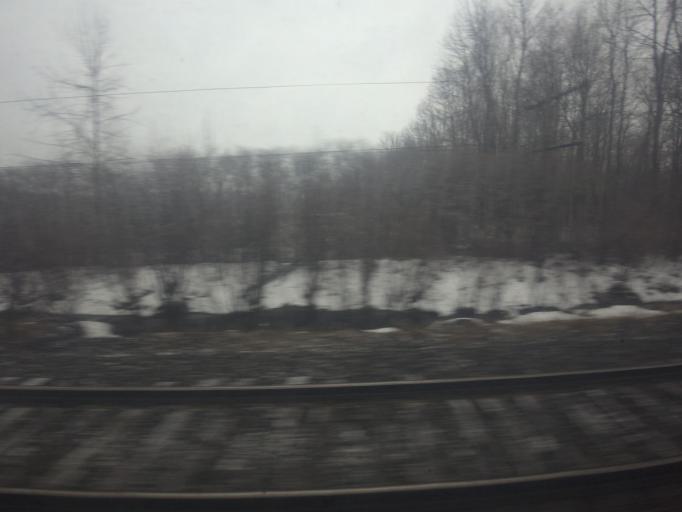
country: CA
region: Ontario
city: Brockville
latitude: 44.5705
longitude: -75.7590
